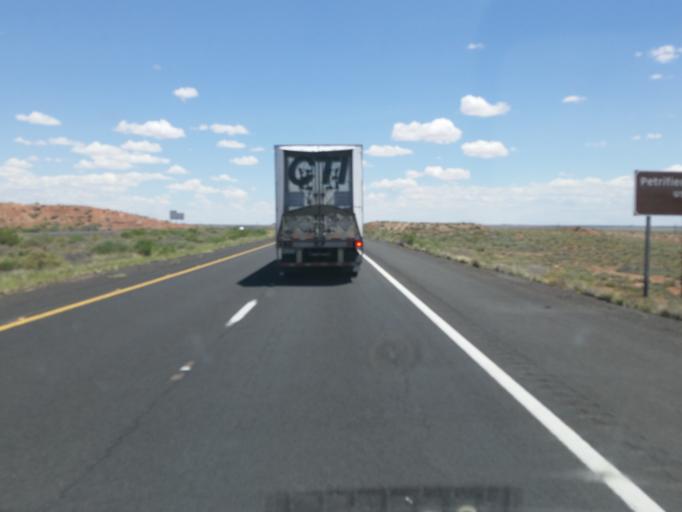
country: US
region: Arizona
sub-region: Navajo County
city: Holbrook
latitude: 34.9149
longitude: -110.2488
